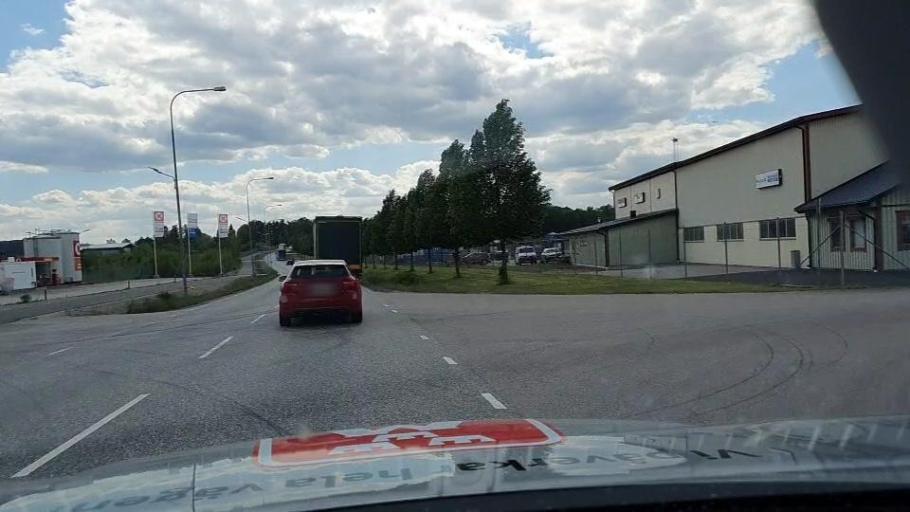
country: SE
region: Kronoberg
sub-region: Ljungby Kommun
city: Ljungby
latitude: 56.8467
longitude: 13.9222
